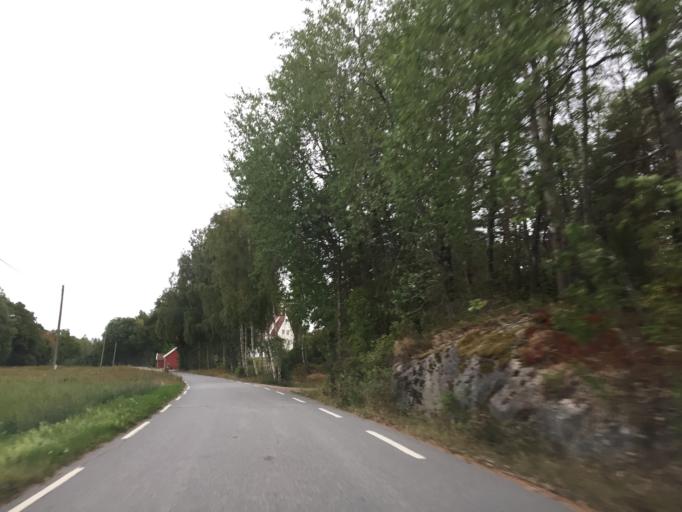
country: NO
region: Ostfold
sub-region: Hvaler
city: Skjaerhalden
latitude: 59.0675
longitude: 11.0049
